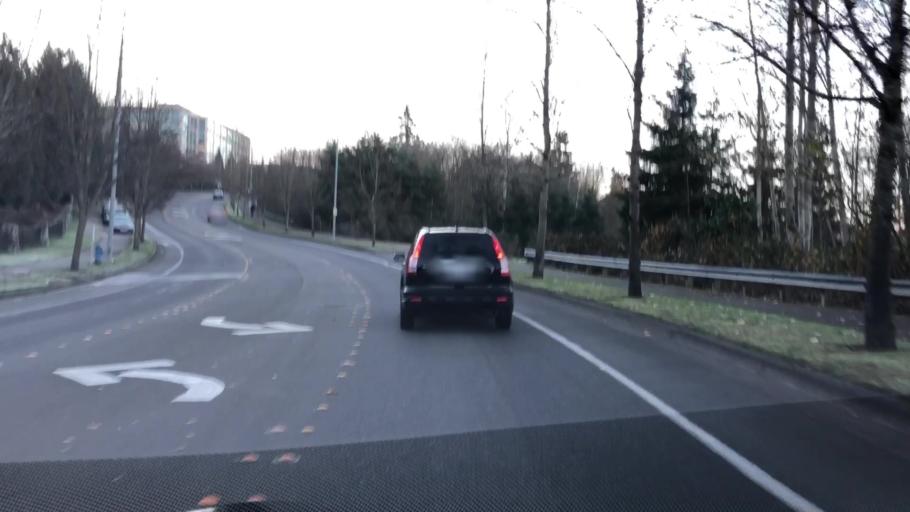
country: US
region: Washington
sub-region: King County
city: Eastgate
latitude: 47.5860
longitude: -122.1558
